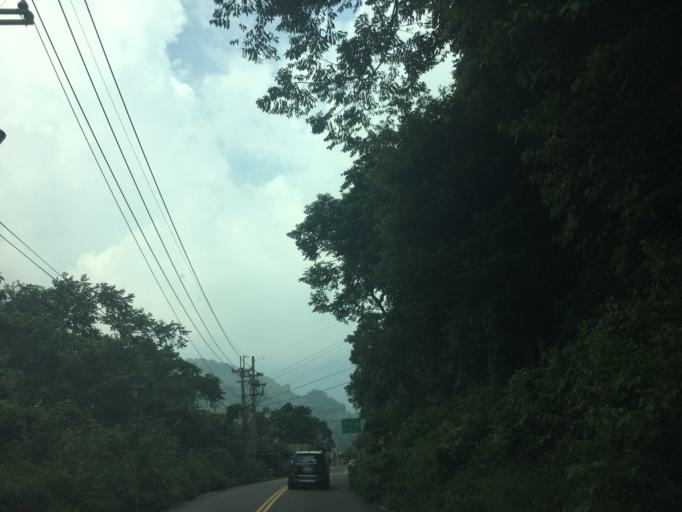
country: TW
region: Taiwan
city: Fengyuan
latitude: 24.2968
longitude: 120.9226
